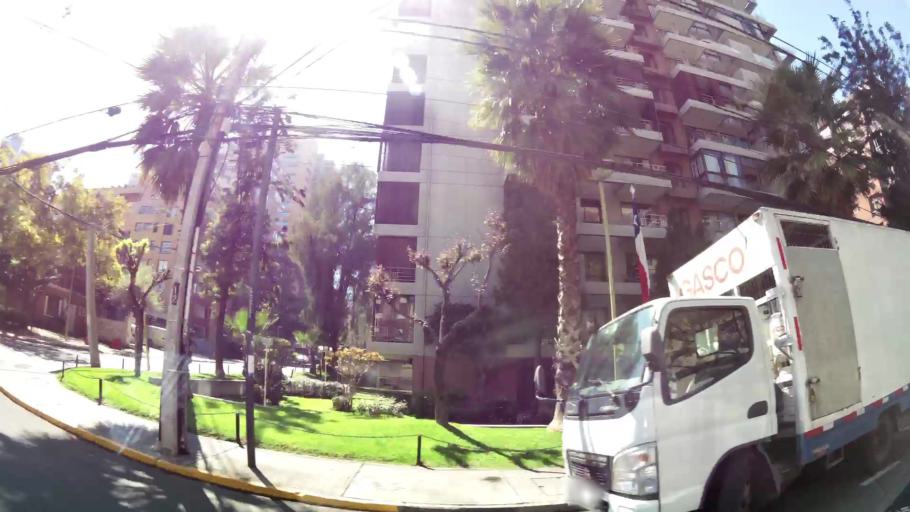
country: CL
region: Santiago Metropolitan
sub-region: Provincia de Santiago
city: Villa Presidente Frei, Nunoa, Santiago, Chile
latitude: -33.4139
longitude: -70.5806
